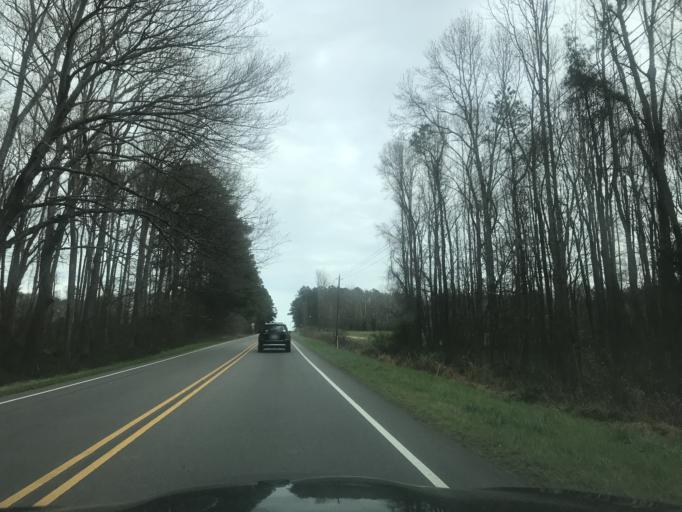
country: US
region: North Carolina
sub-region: Franklin County
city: Franklinton
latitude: 36.0896
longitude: -78.3917
